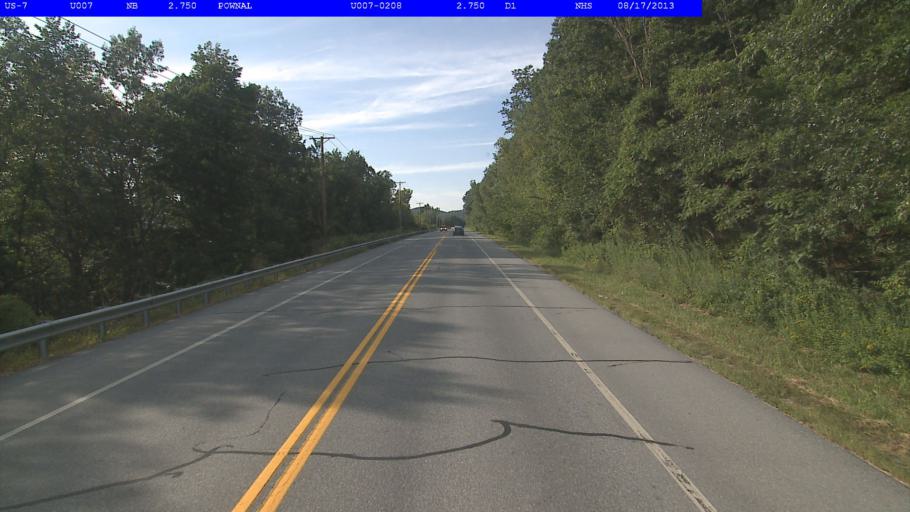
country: US
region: Massachusetts
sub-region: Berkshire County
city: Williamstown
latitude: 42.7750
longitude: -73.2394
